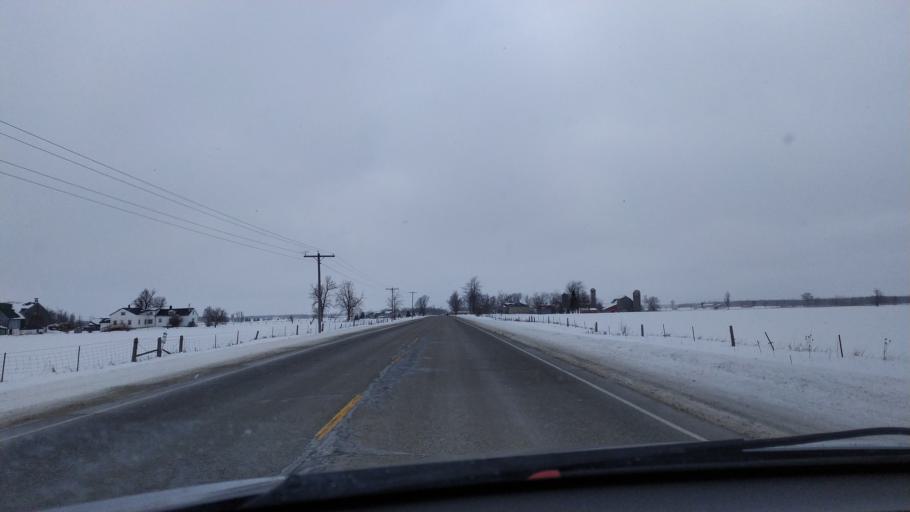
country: CA
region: Ontario
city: North Perth
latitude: 43.5788
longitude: -80.8518
